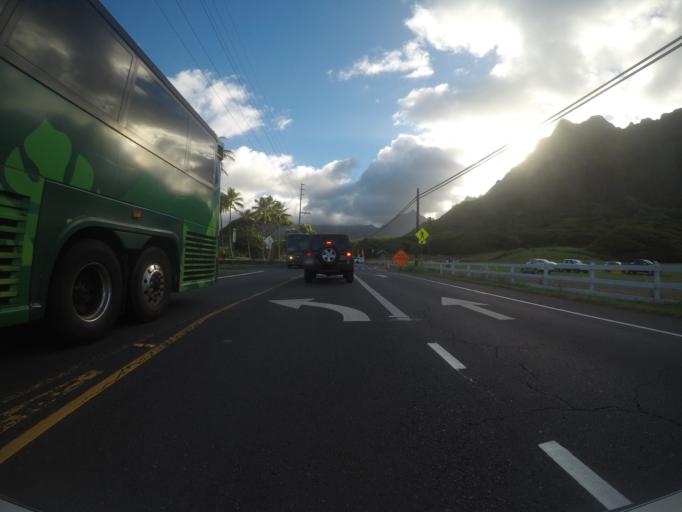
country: US
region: Hawaii
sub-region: Honolulu County
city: Ka'a'awa
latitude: 21.5172
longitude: -157.8375
